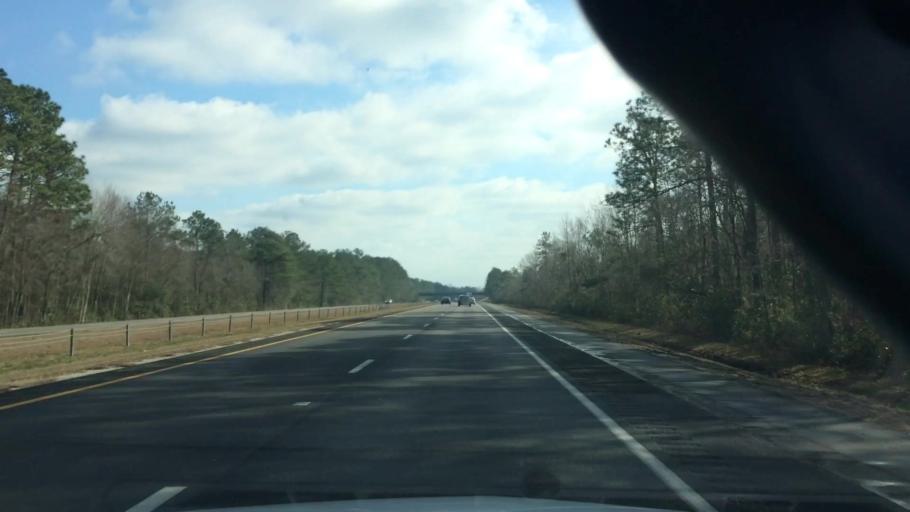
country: US
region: North Carolina
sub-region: Pender County
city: Burgaw
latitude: 34.6168
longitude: -77.9256
